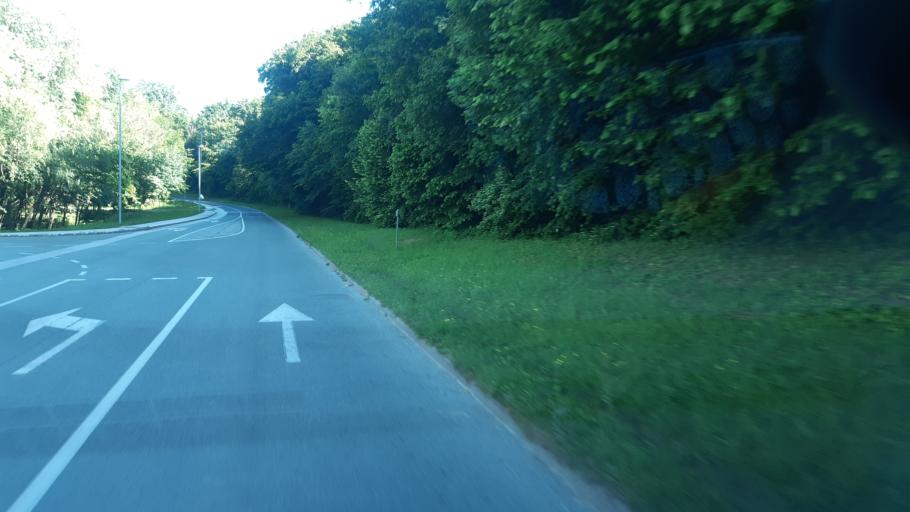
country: SI
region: Kranj
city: Kranj
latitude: 46.2198
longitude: 14.3680
